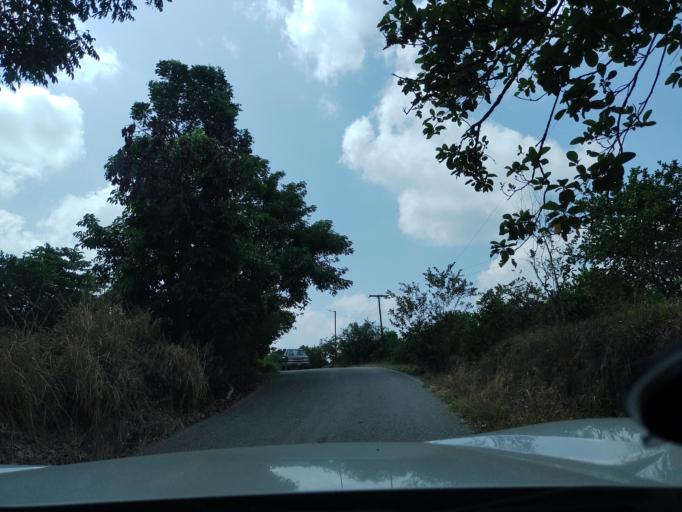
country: MX
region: Veracruz
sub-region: Martinez de la Torre
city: La Union Paso Largo
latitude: 20.1812
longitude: -97.0347
